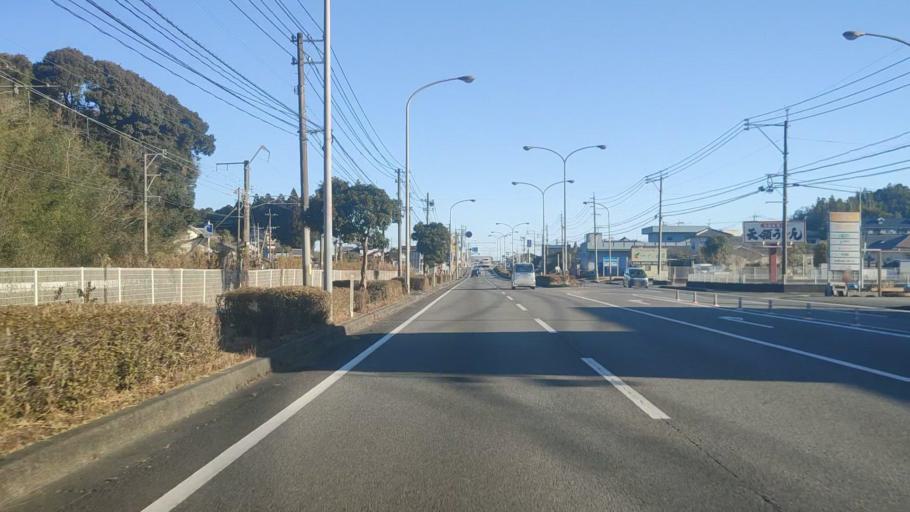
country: JP
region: Miyazaki
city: Nobeoka
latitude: 32.4552
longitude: 131.6434
